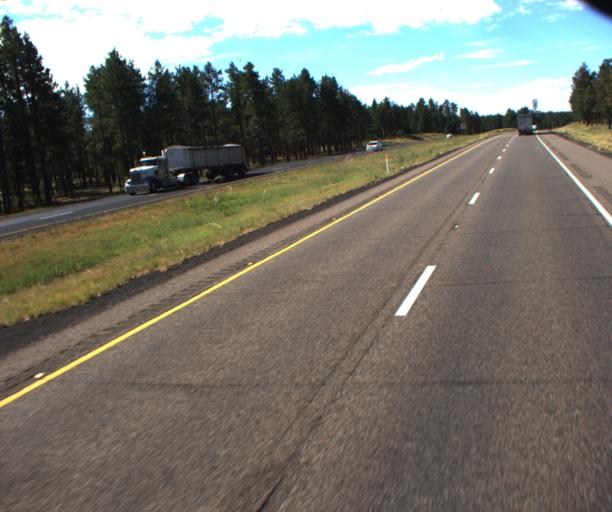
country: US
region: Arizona
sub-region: Coconino County
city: Sedona
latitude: 34.8401
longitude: -111.6042
